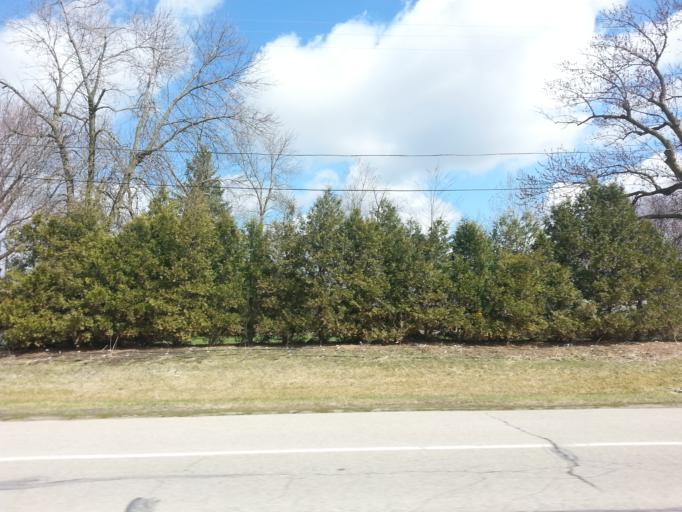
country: US
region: Minnesota
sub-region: Dodge County
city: Dodge Center
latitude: 44.1436
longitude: -92.8996
